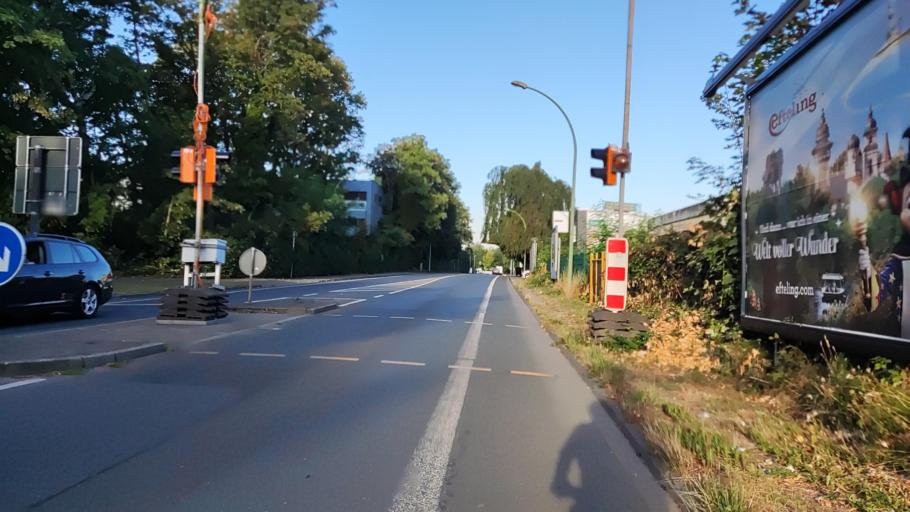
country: DE
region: North Rhine-Westphalia
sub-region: Regierungsbezirk Arnsberg
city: Herne
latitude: 51.5494
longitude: 7.2406
